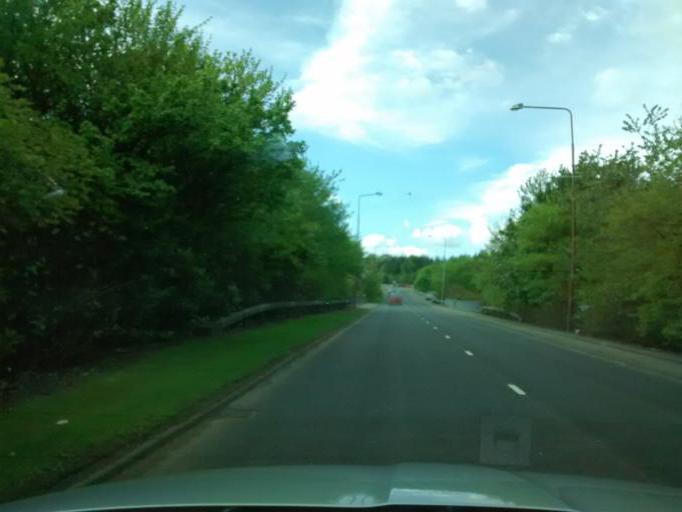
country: GB
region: Scotland
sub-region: West Lothian
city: West Calder
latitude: 55.8828
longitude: -3.5567
